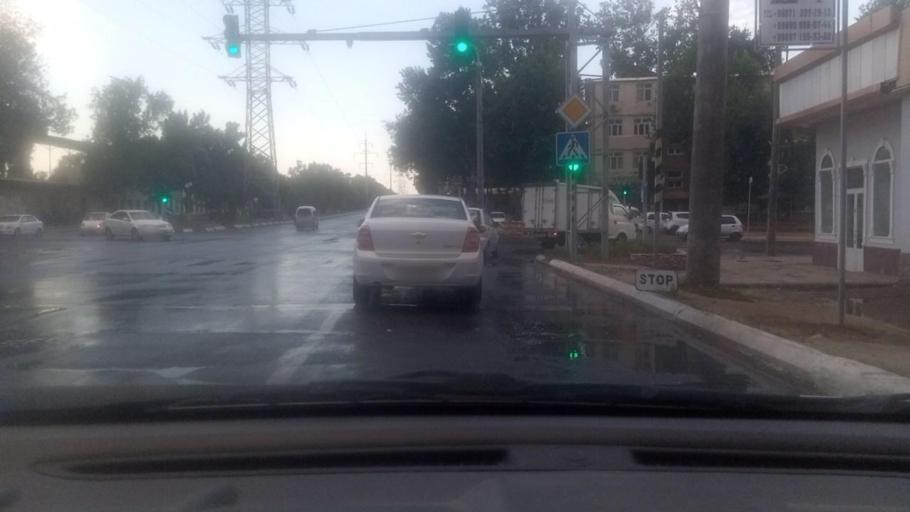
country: UZ
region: Toshkent Shahri
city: Tashkent
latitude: 41.2981
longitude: 69.1938
